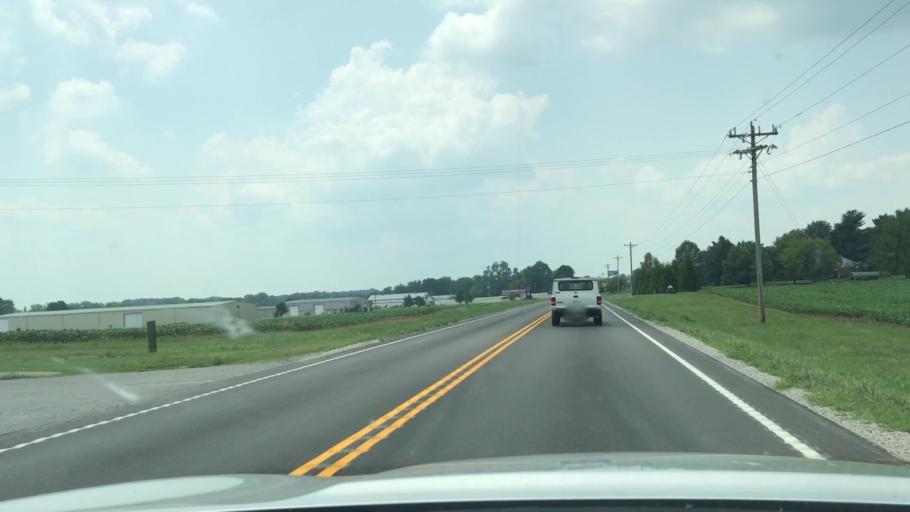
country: US
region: Kentucky
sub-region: Todd County
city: Guthrie
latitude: 36.6504
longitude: -87.1896
